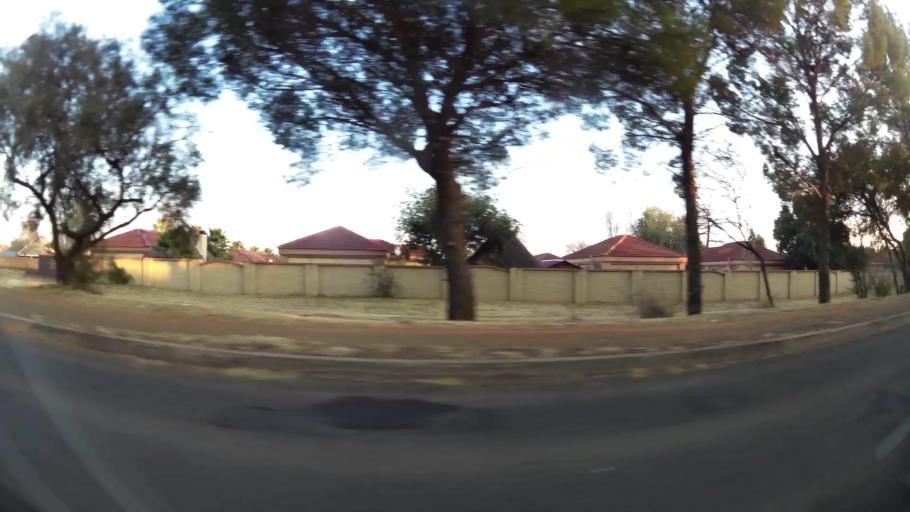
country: ZA
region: Orange Free State
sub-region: Mangaung Metropolitan Municipality
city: Bloemfontein
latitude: -29.0912
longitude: 26.1511
